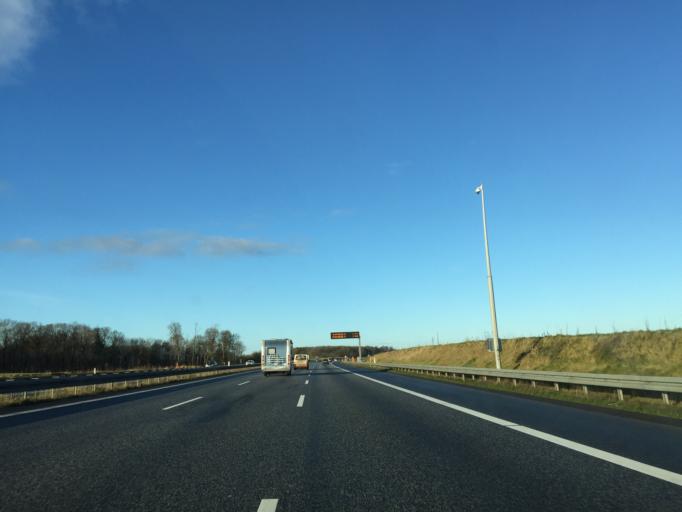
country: DK
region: South Denmark
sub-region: Vejle Kommune
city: Borkop
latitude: 55.6241
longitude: 9.5711
